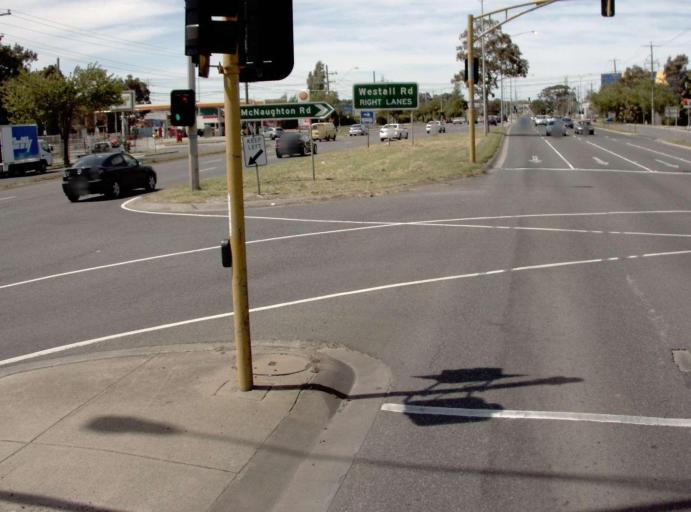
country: AU
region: Victoria
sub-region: Monash
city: Clayton
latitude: -37.9232
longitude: 145.1412
